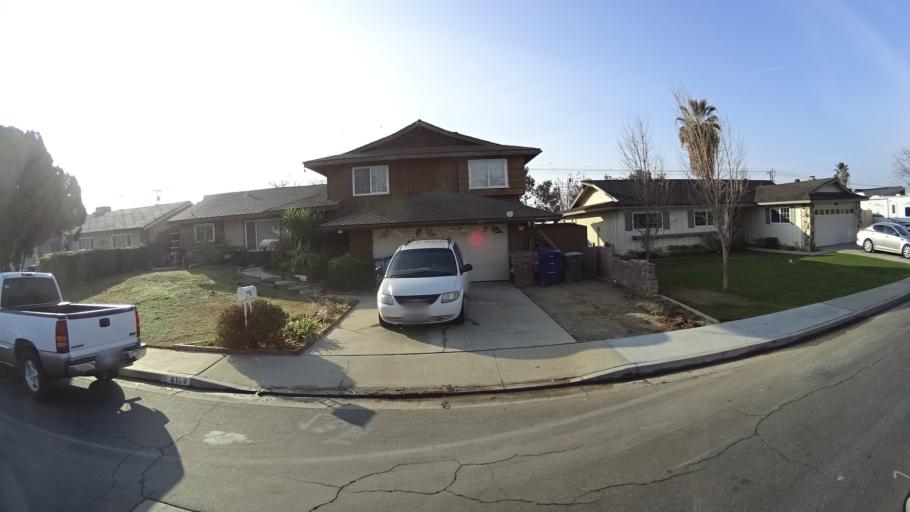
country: US
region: California
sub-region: Kern County
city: Oildale
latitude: 35.3983
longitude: -118.9471
